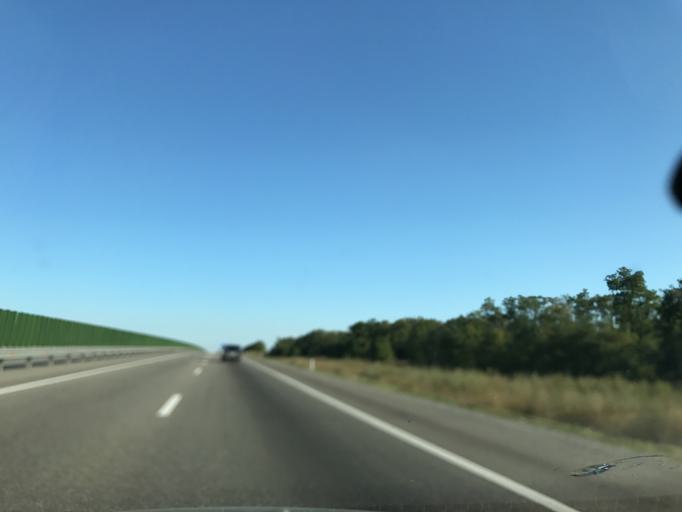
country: RU
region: Rostov
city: Glubokiy
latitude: 48.5763
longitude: 40.3519
